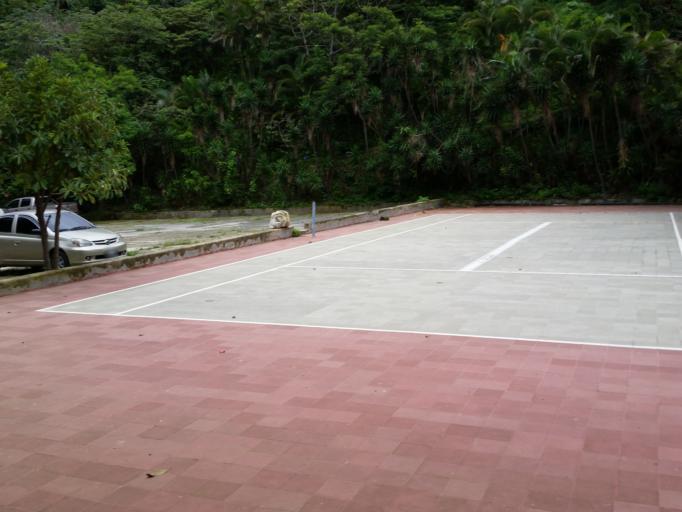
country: NI
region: Managua
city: El Crucero
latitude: 11.9911
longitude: -86.2969
